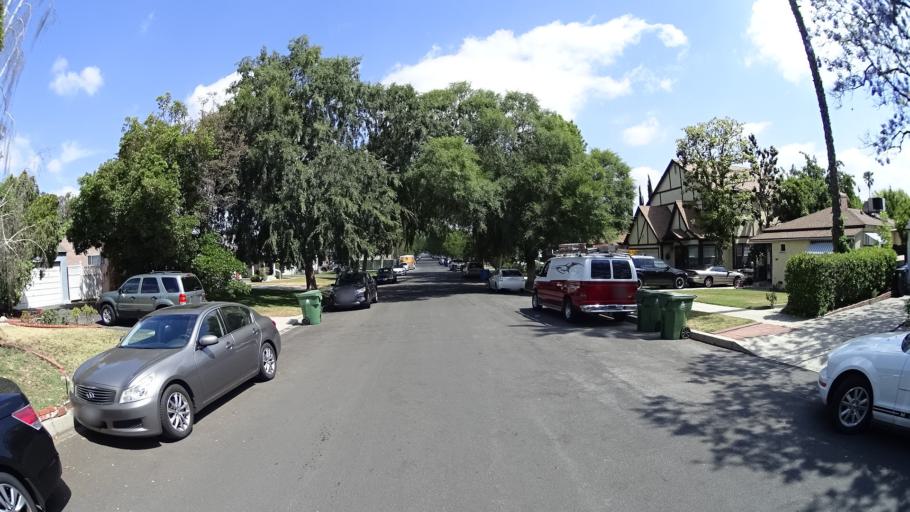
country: US
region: California
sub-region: Los Angeles County
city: Universal City
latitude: 34.1580
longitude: -118.3551
